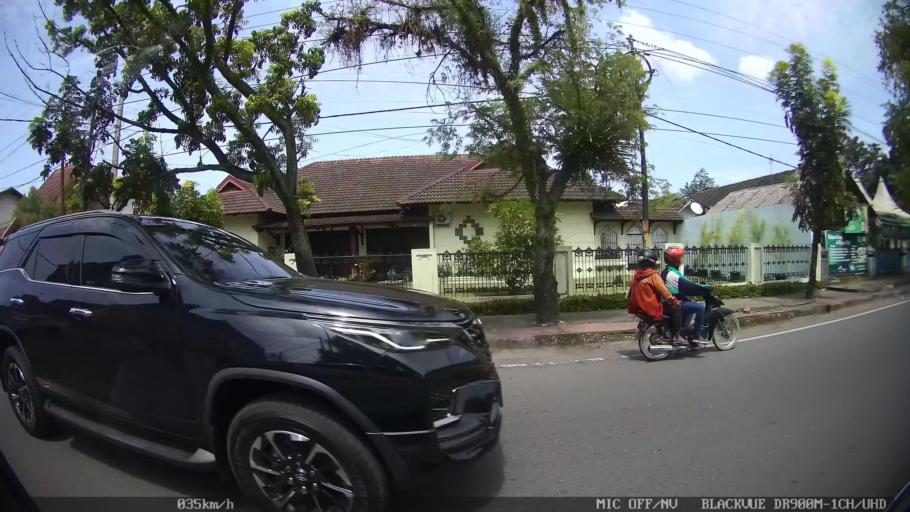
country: ID
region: North Sumatra
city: Medan
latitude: 3.5857
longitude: 98.6573
